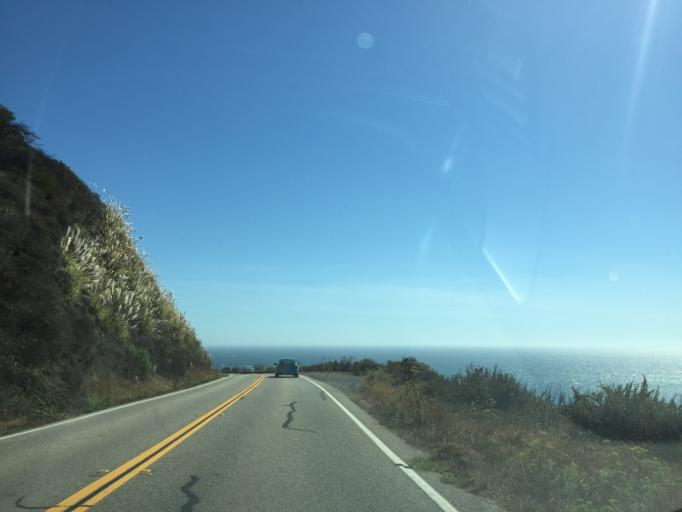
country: US
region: California
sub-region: Monterey County
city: Greenfield
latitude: 36.0269
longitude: -121.5731
